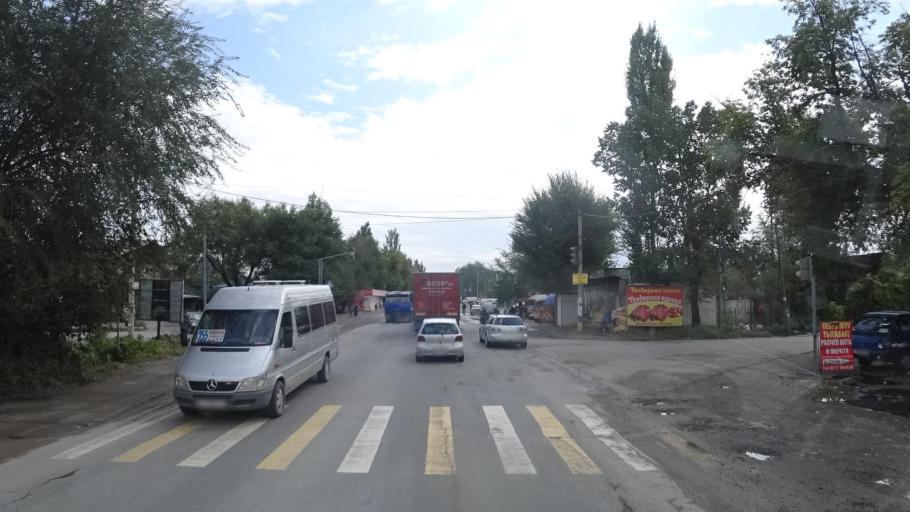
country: KG
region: Chuy
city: Lebedinovka
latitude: 42.8775
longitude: 74.7093
